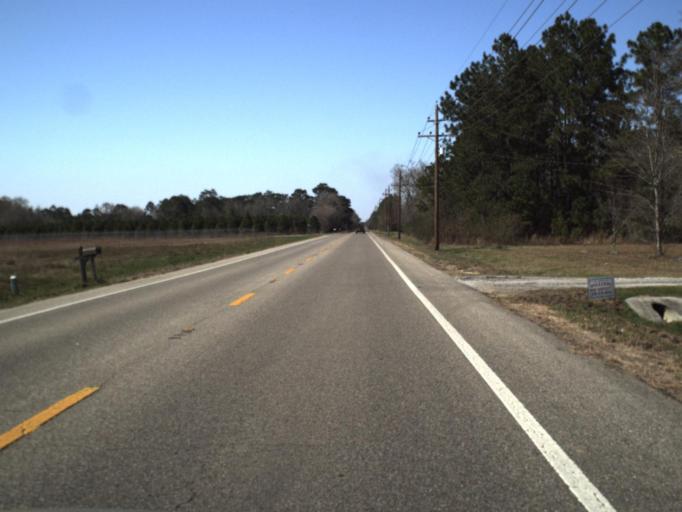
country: US
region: Florida
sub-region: Calhoun County
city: Blountstown
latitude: 30.4928
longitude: -85.1107
